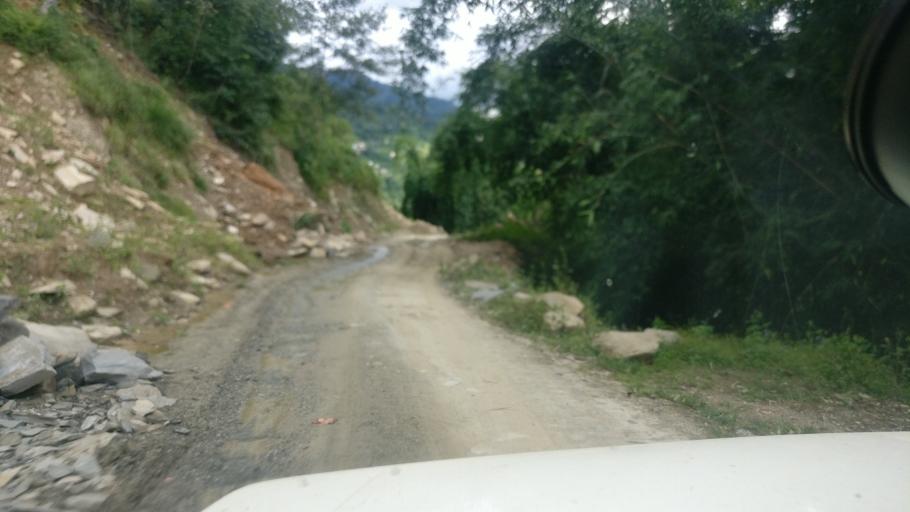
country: NP
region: Western Region
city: Baglung
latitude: 28.2606
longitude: 83.6508
